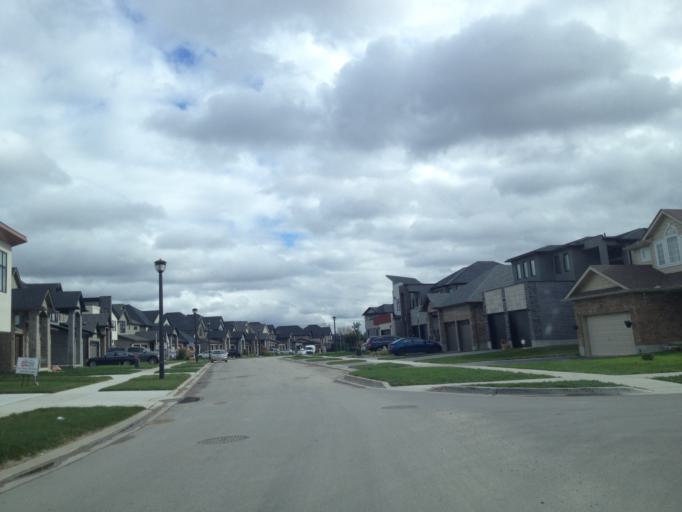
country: CA
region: Ontario
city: London
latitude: 43.0174
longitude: -81.3263
